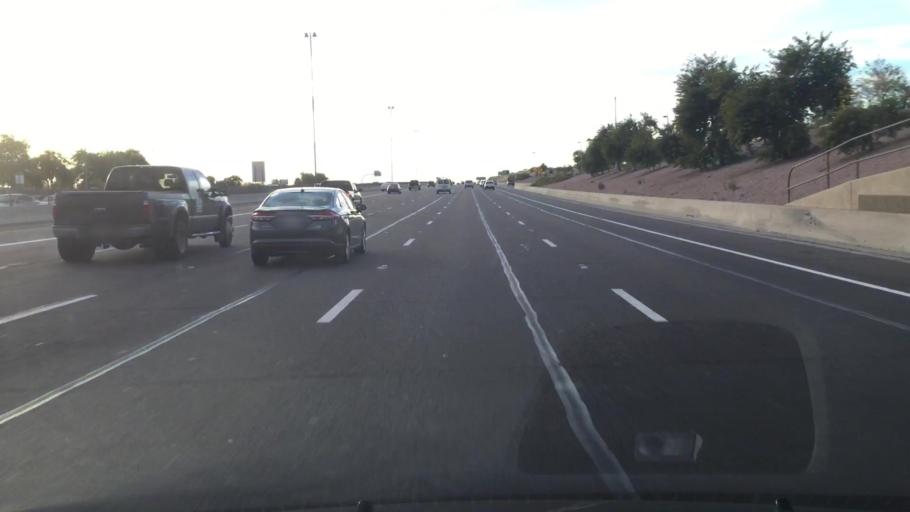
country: US
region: Arizona
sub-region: Maricopa County
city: Mesa
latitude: 33.3830
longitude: -111.8249
